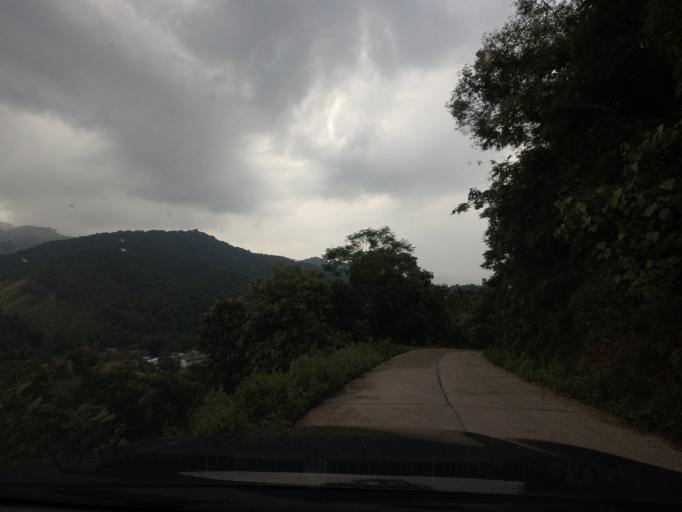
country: TH
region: Nan
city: Bo Kluea
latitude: 19.3509
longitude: 101.1621
